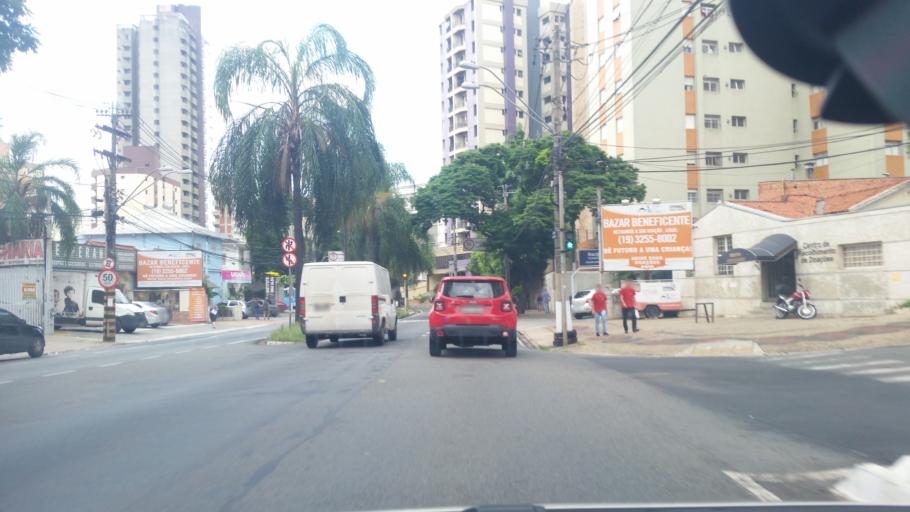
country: BR
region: Sao Paulo
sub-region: Campinas
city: Campinas
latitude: -22.8981
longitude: -47.0585
